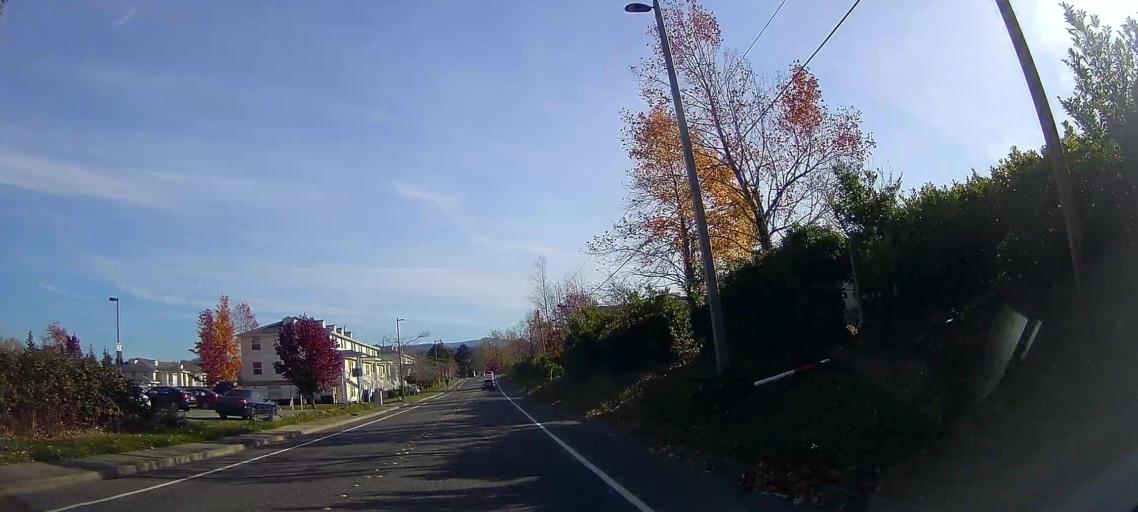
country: US
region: Washington
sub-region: Whatcom County
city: Bellingham
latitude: 48.7751
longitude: -122.4602
